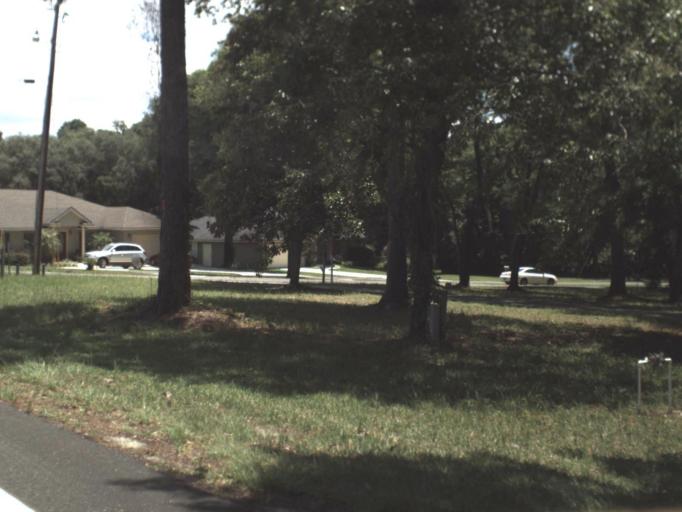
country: US
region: Florida
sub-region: Clay County
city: Keystone Heights
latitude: 29.7620
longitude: -82.0552
